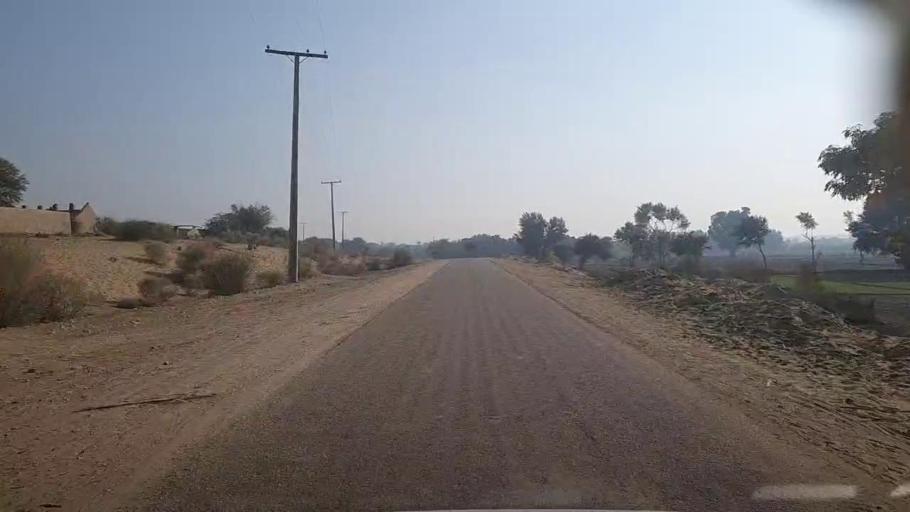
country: PK
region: Sindh
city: Kandiari
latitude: 26.8353
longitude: 68.4896
